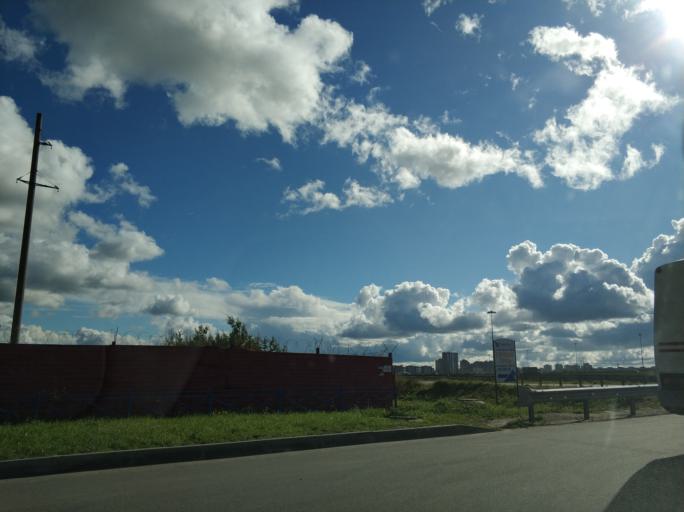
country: RU
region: Leningrad
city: Bugry
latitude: 60.0597
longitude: 30.3927
